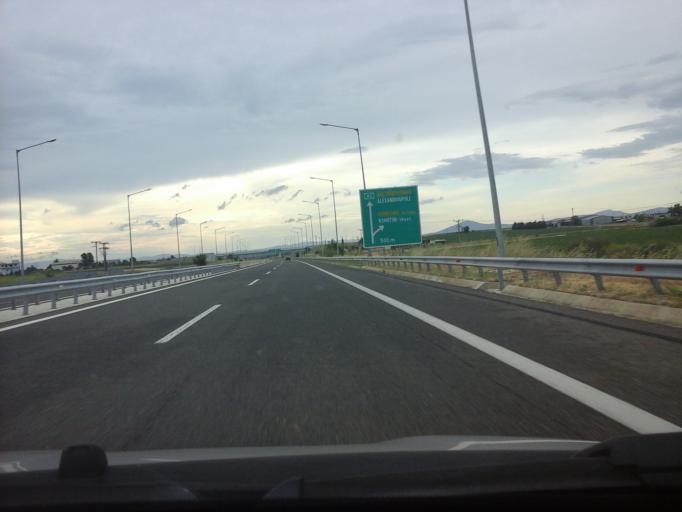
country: GR
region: East Macedonia and Thrace
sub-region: Nomos Rodopis
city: Komotini
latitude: 41.1063
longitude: 25.3467
